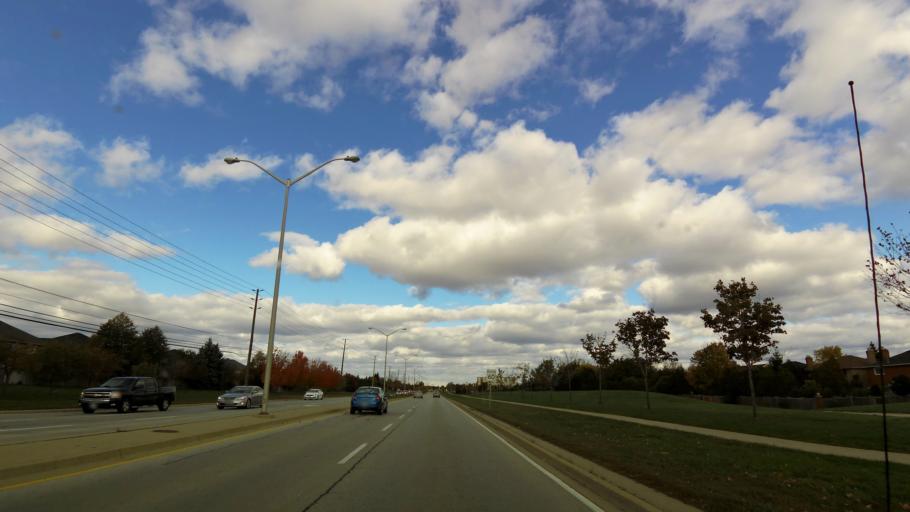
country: CA
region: Ontario
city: Oakville
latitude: 43.4416
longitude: -79.7387
